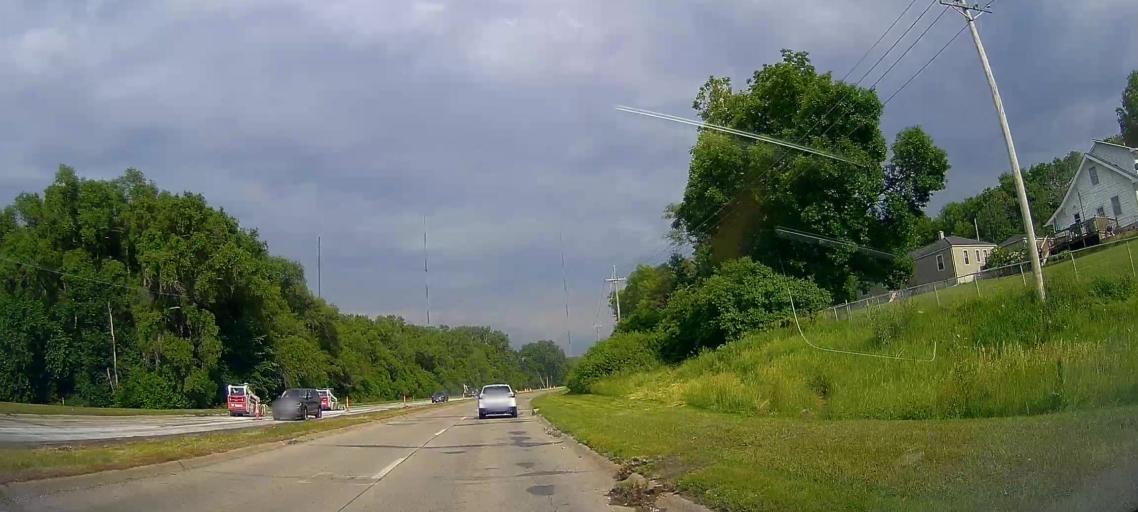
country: US
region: Nebraska
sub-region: Douglas County
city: Ralston
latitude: 41.3096
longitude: -96.0432
